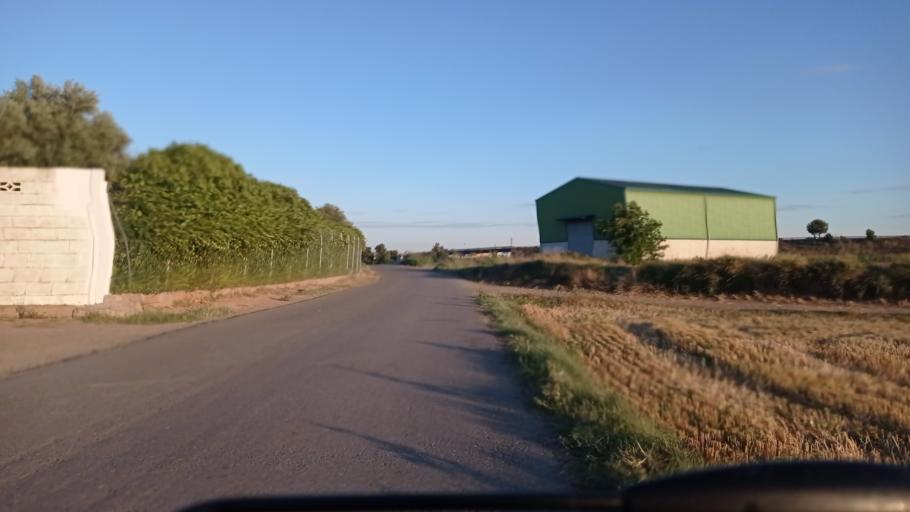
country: ES
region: Aragon
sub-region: Provincia de Zaragoza
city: Oliver-Valdefierro, Oliver, Valdefierro
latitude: 41.6817
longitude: -0.9339
